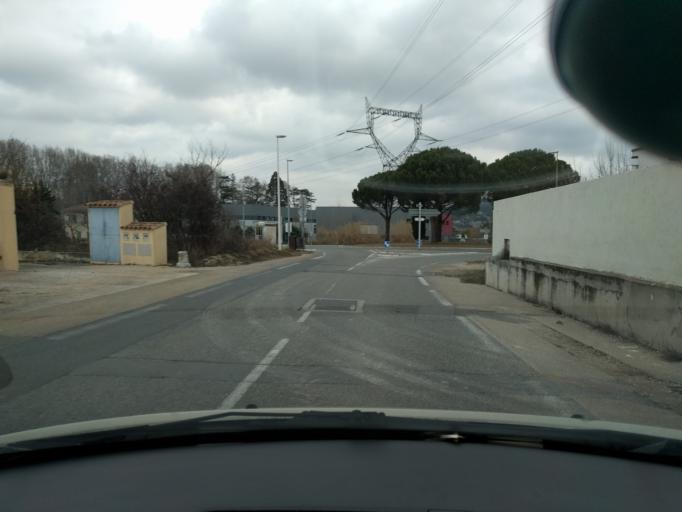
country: FR
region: Provence-Alpes-Cote d'Azur
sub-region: Departement des Bouches-du-Rhone
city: Bouc-Bel-Air
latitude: 43.4356
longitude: 5.4039
